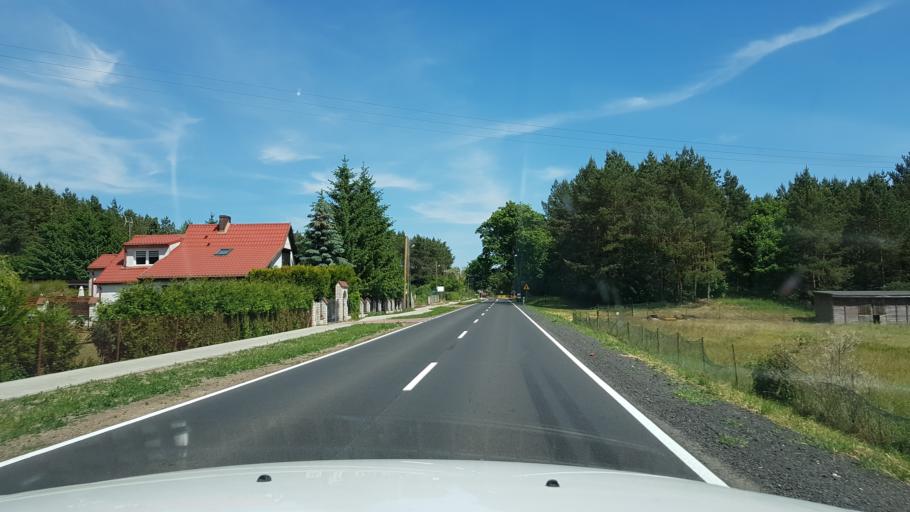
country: PL
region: West Pomeranian Voivodeship
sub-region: Powiat gryfinski
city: Chojna
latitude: 52.9605
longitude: 14.4734
